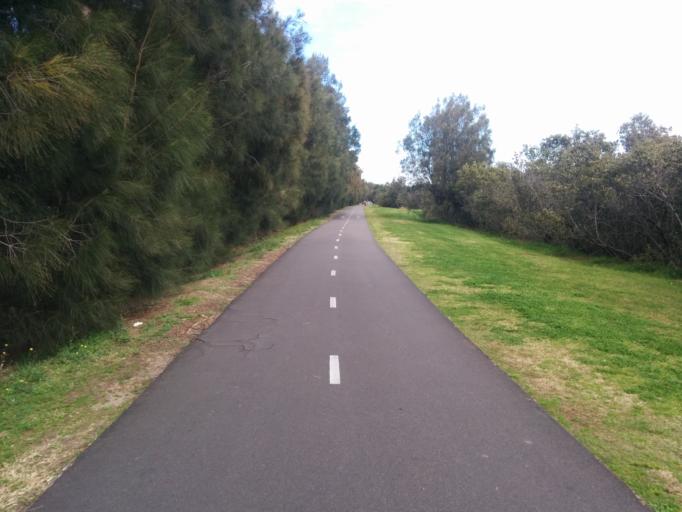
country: AU
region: New South Wales
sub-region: Canada Bay
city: Concord West
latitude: -33.8417
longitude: 151.0827
